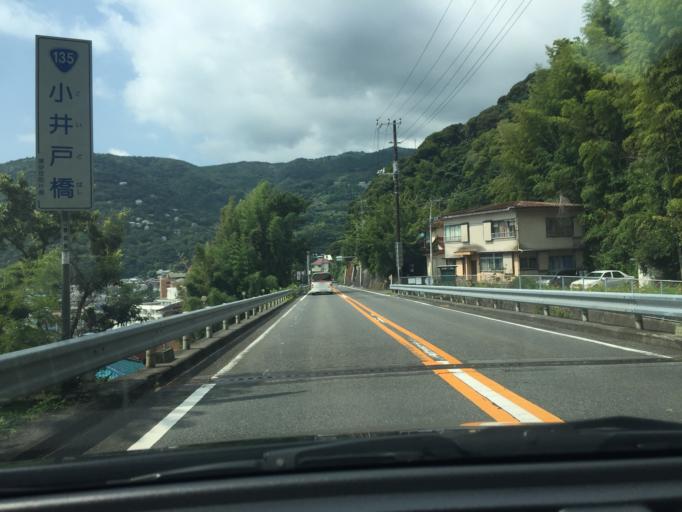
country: JP
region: Shizuoka
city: Ito
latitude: 34.8075
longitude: 139.0648
